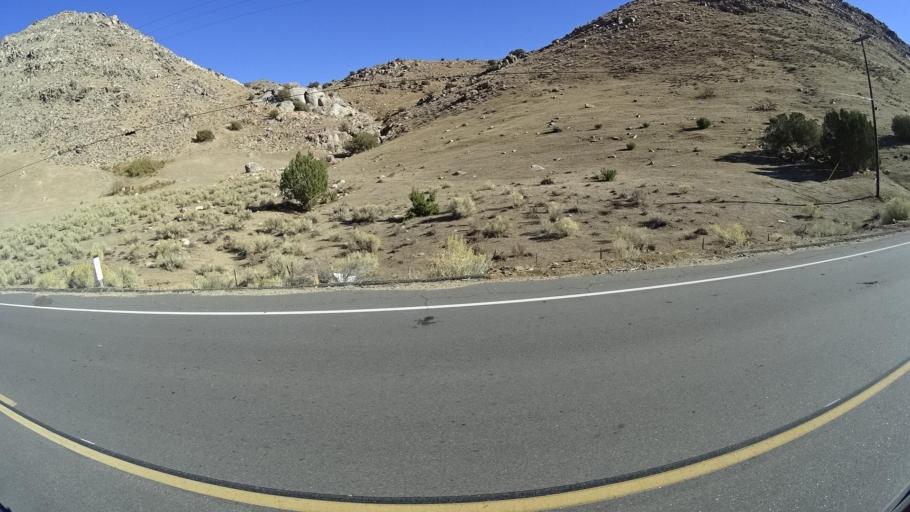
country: US
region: California
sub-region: Kern County
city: Wofford Heights
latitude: 35.7143
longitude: -118.4187
